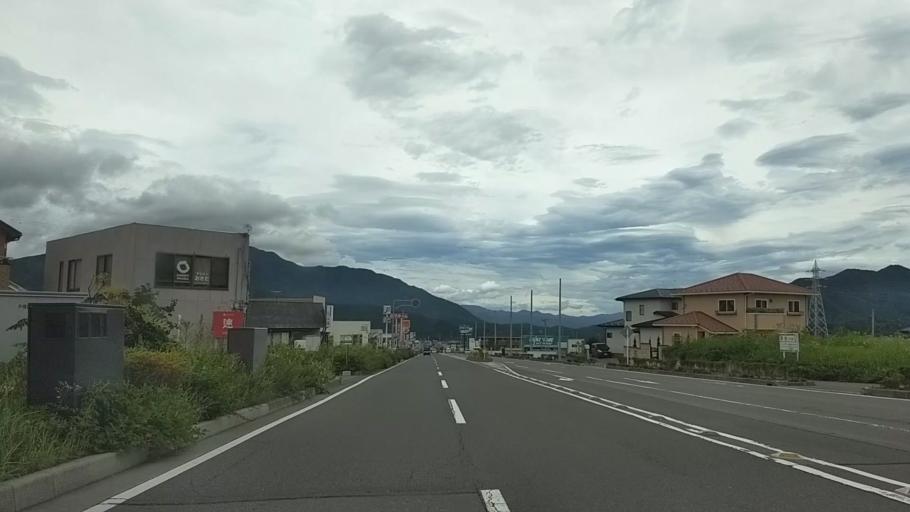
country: JP
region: Yamanashi
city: Fujikawaguchiko
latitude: 35.4714
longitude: 138.8065
